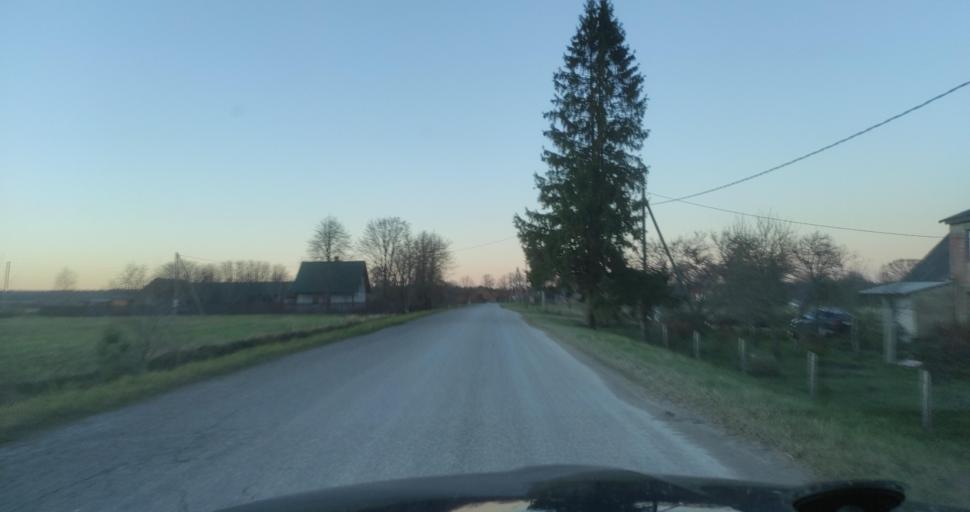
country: LV
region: Dundaga
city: Dundaga
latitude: 57.3726
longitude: 22.2323
